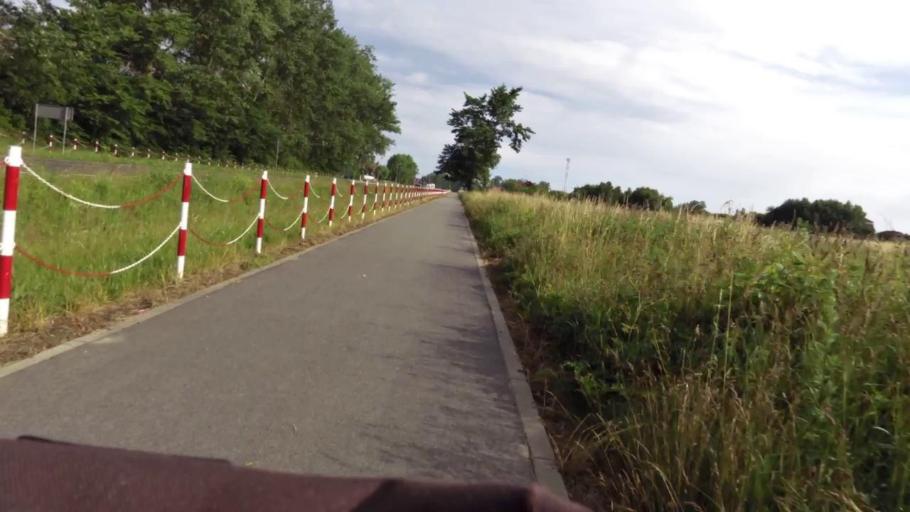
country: PL
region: West Pomeranian Voivodeship
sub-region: Powiat kamienski
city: Dziwnow
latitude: 54.0231
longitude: 14.8094
